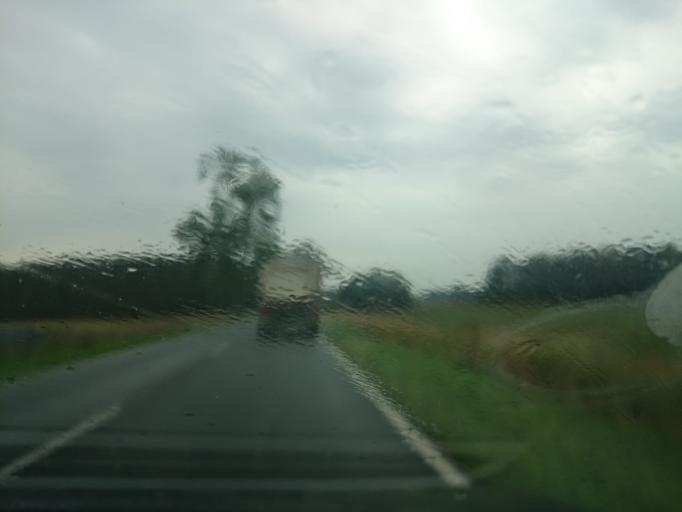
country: DE
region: Brandenburg
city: Gransee
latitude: 52.8747
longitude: 13.1633
